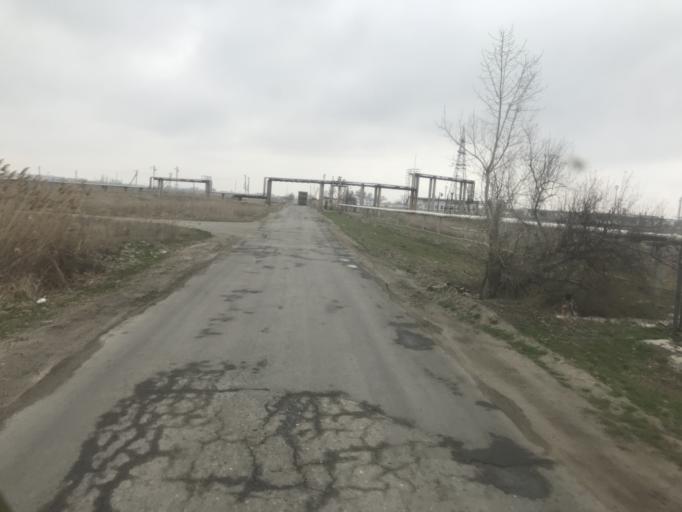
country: RU
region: Volgograd
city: Svetlyy Yar
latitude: 48.5130
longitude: 44.6351
